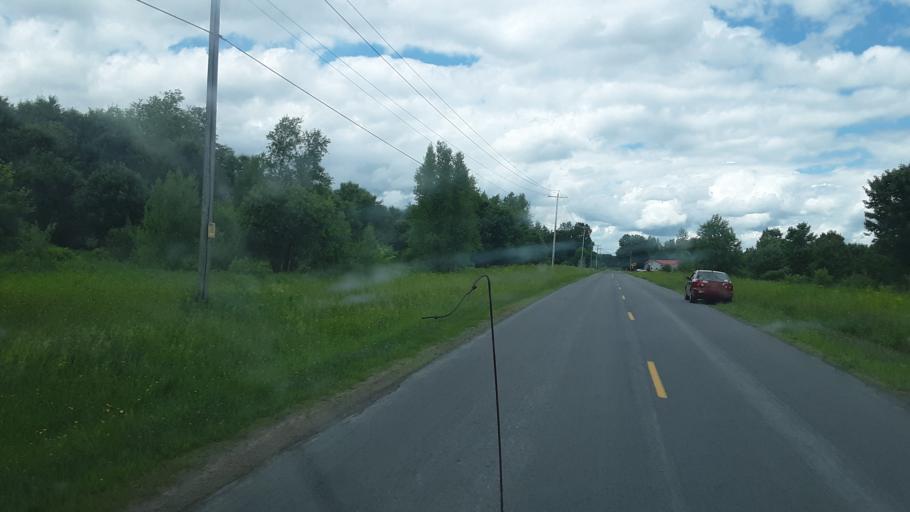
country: US
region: New York
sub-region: Oneida County
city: Rome
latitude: 43.3617
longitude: -75.5505
